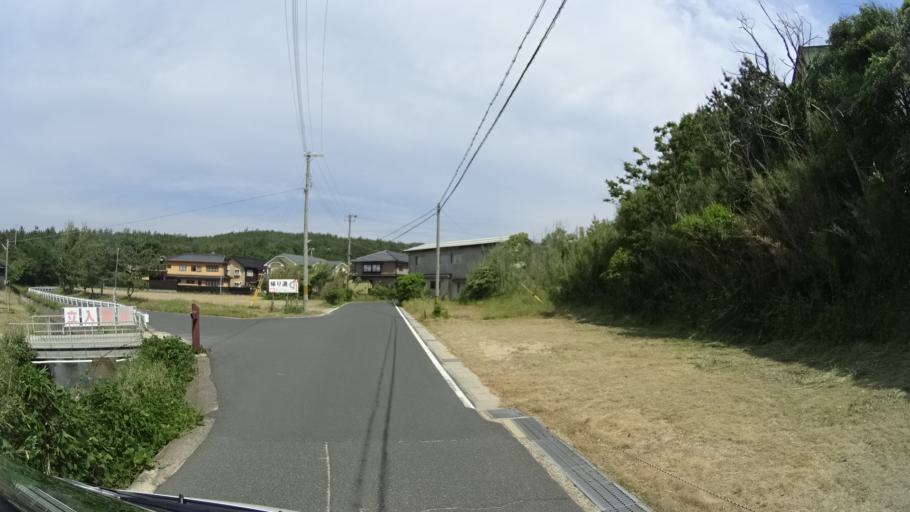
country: JP
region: Kyoto
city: Miyazu
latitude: 35.7012
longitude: 135.0521
